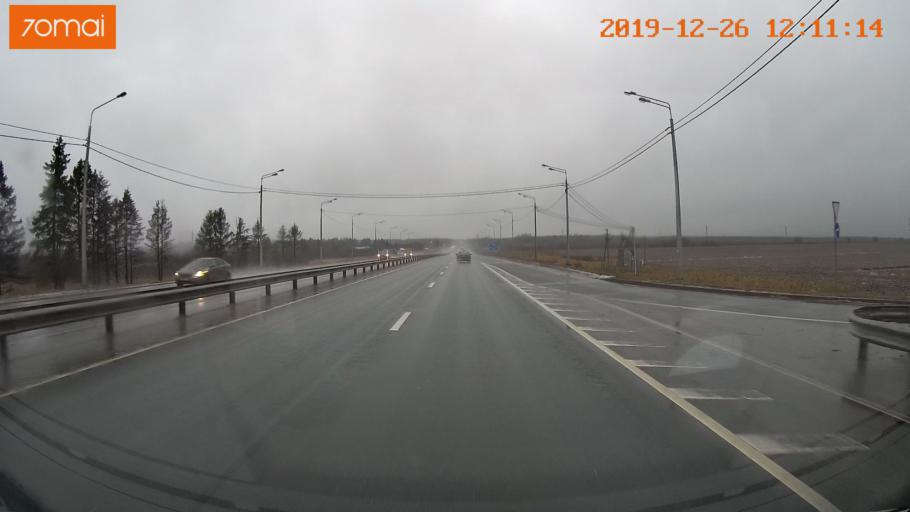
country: RU
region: Vologda
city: Tonshalovo
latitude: 59.2501
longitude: 37.9730
